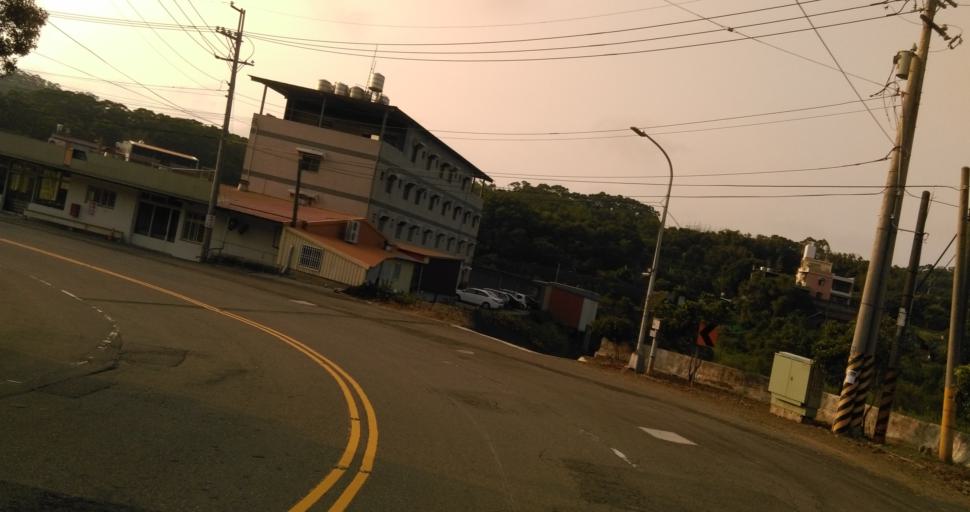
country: TW
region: Taiwan
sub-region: Hsinchu
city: Hsinchu
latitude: 24.7550
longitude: 120.9410
